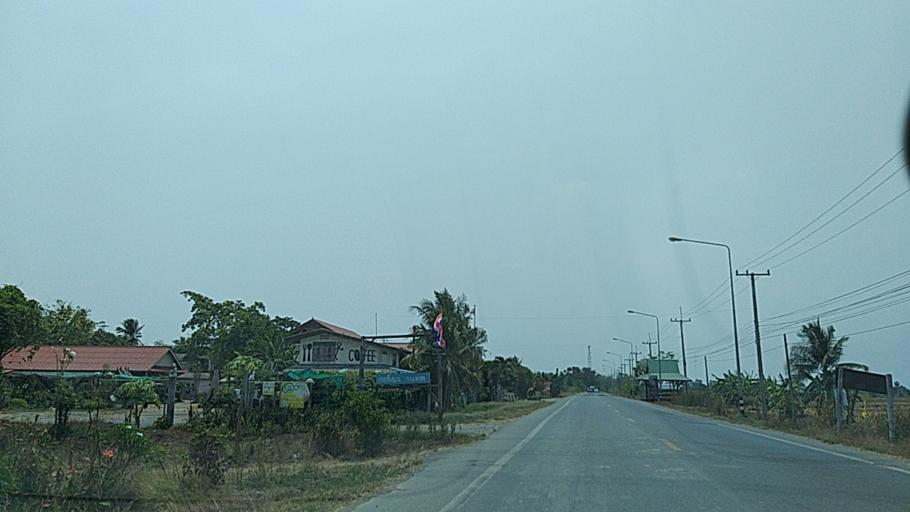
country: TH
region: Chachoengsao
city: Bang Nam Priao
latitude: 13.8888
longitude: 100.9702
